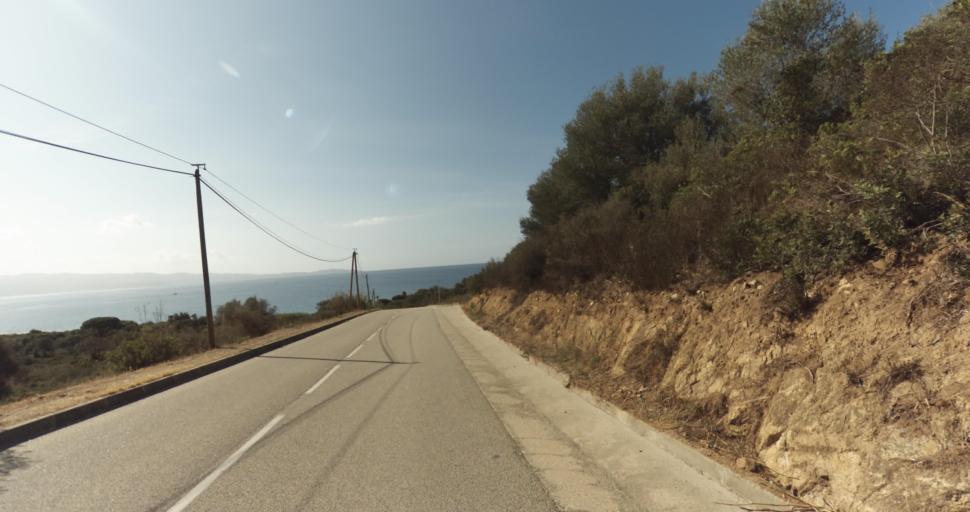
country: FR
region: Corsica
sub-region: Departement de la Corse-du-Sud
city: Ajaccio
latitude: 41.9135
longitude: 8.6437
